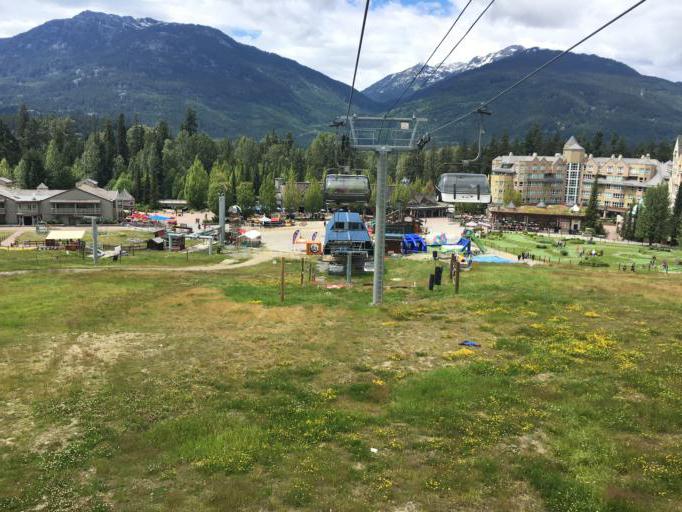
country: CA
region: British Columbia
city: Whistler
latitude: 50.1149
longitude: -122.9460
